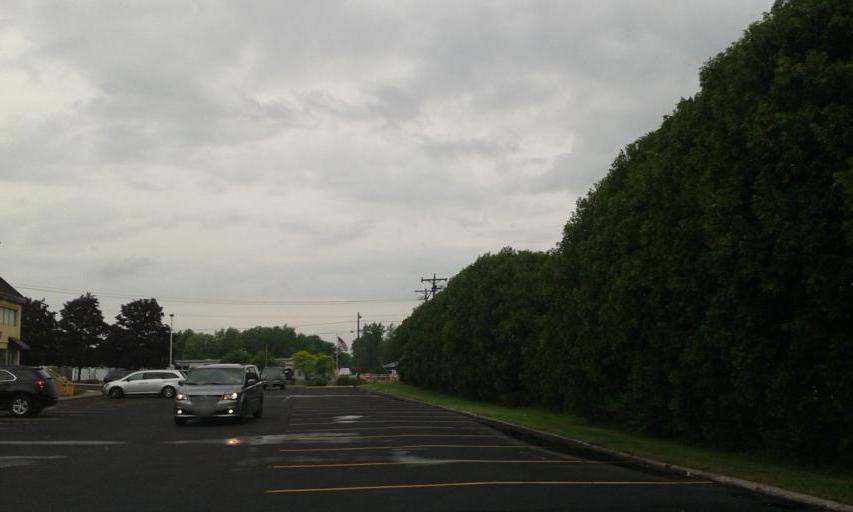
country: US
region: New York
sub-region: Onondaga County
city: Seneca Knolls
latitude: 43.1158
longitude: -76.2697
